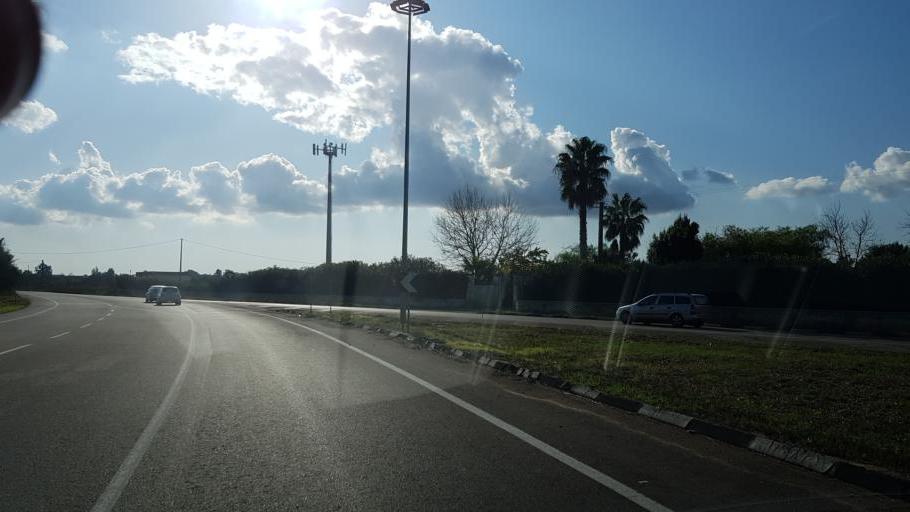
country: IT
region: Apulia
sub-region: Provincia di Lecce
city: Salice Salentino
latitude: 40.3739
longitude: 17.9671
